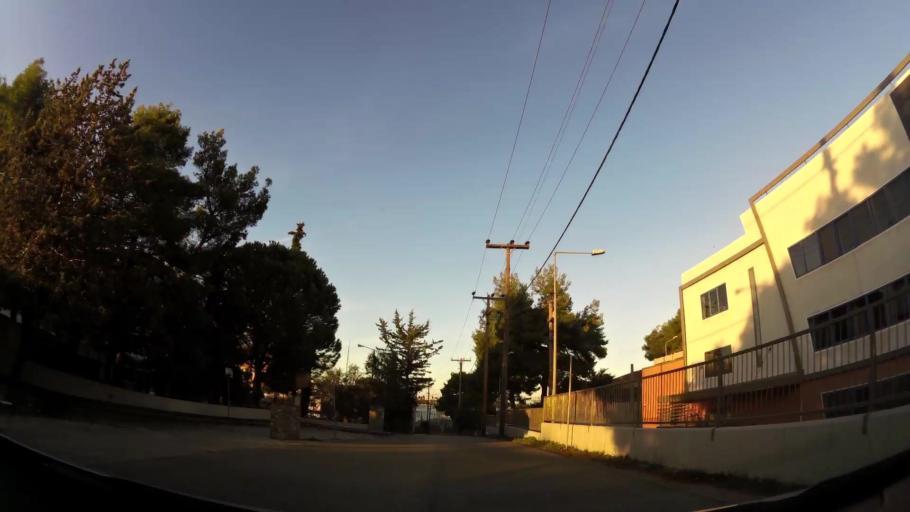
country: GR
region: Attica
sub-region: Nomarchia Anatolikis Attikis
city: Kryoneri
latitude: 38.1386
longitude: 23.8373
